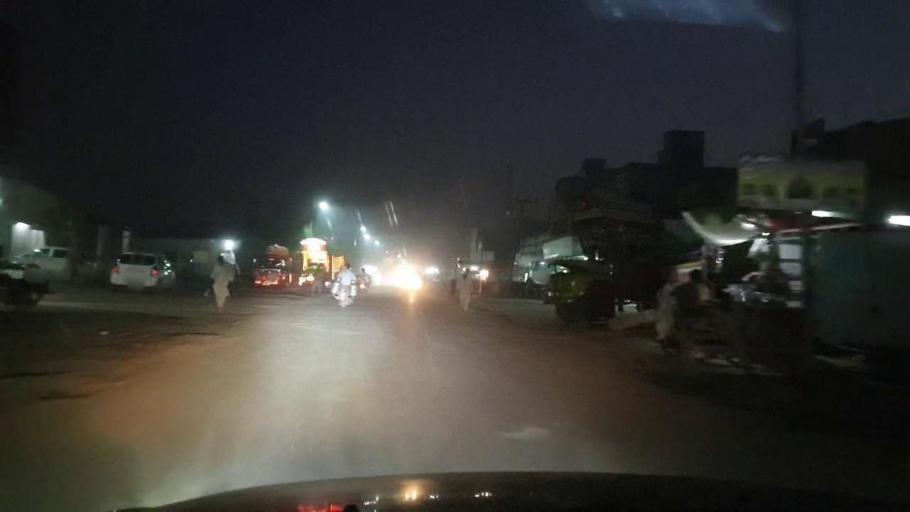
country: PK
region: Sindh
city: Chambar
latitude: 25.2994
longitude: 68.8108
